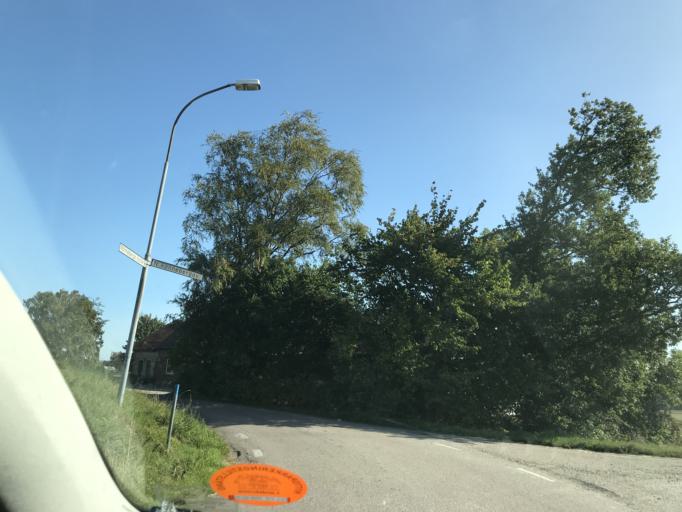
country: SE
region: Skane
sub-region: Landskrona
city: Asmundtorp
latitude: 55.9072
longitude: 12.9480
